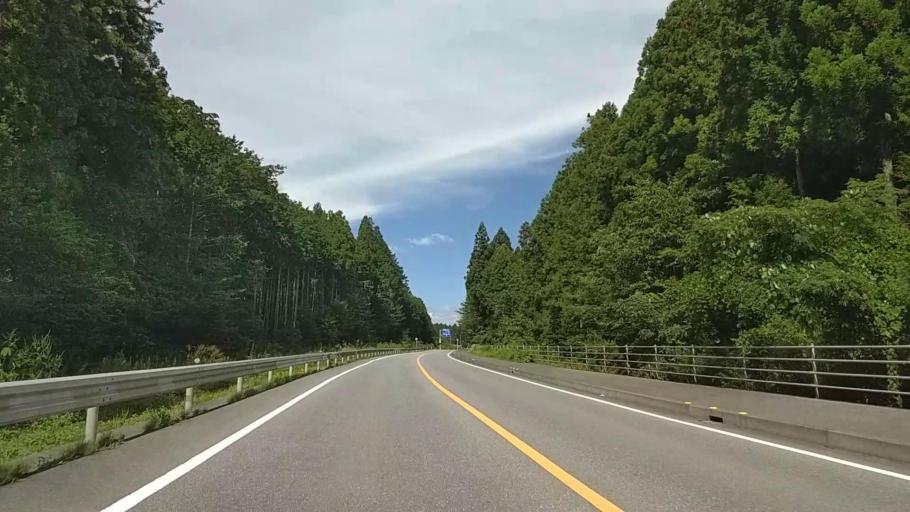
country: JP
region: Tochigi
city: Imaichi
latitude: 36.7029
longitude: 139.7511
